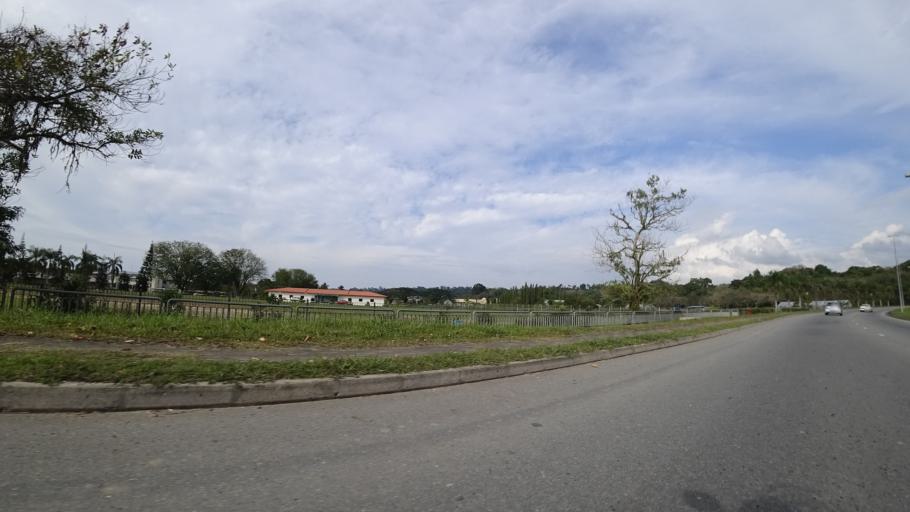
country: BN
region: Brunei and Muara
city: Bandar Seri Begawan
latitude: 4.8952
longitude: 114.8504
